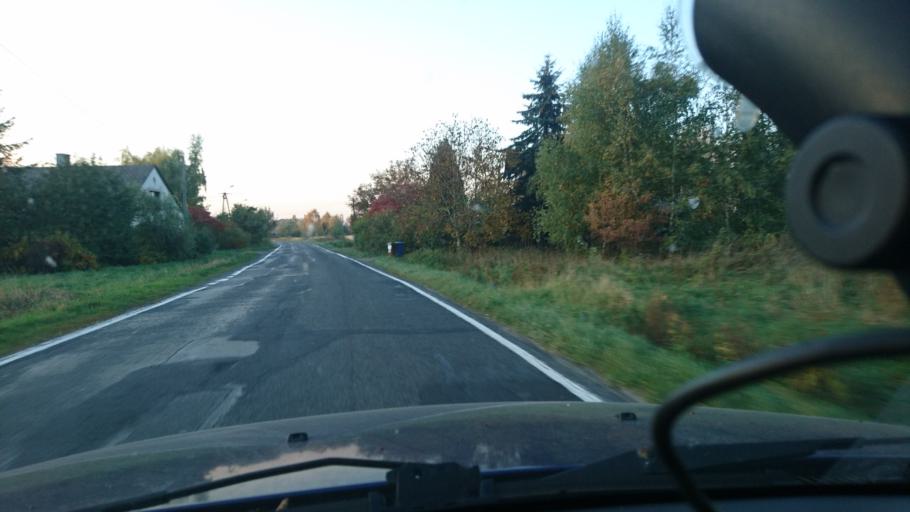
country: PL
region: Silesian Voivodeship
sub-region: Powiat bielski
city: Kozy
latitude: 49.8480
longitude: 19.1164
